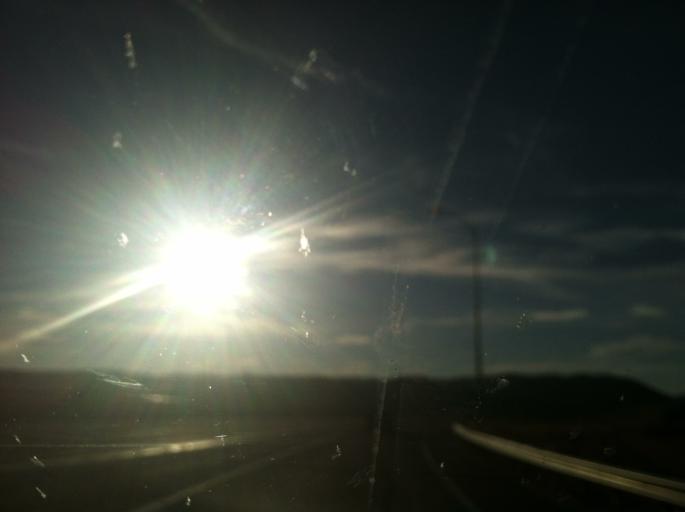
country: US
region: Montana
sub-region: Granite County
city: Philipsburg
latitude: 46.6722
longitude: -113.1577
